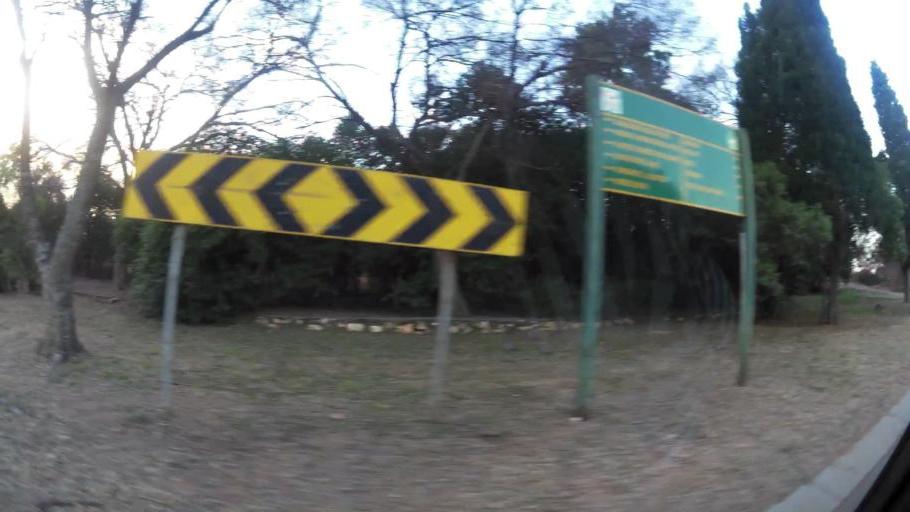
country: ZA
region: Gauteng
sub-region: City of Johannesburg Metropolitan Municipality
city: Midrand
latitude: -26.0087
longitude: 28.0551
